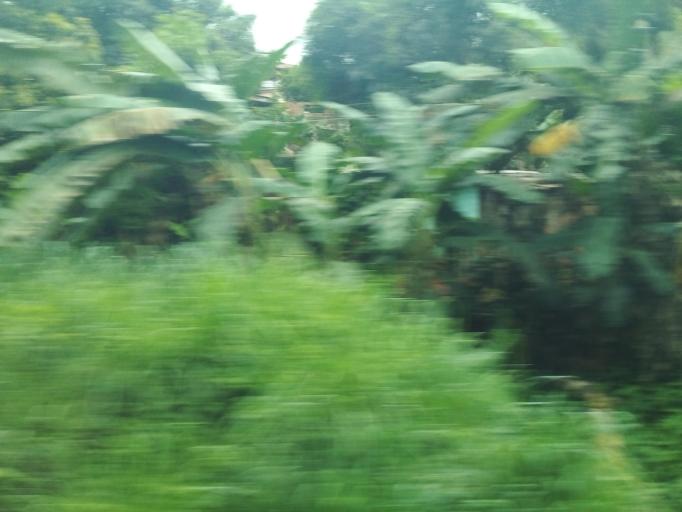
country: BR
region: Minas Gerais
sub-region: Rio Piracicaba
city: Rio Piracicaba
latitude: -19.9024
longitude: -43.1470
